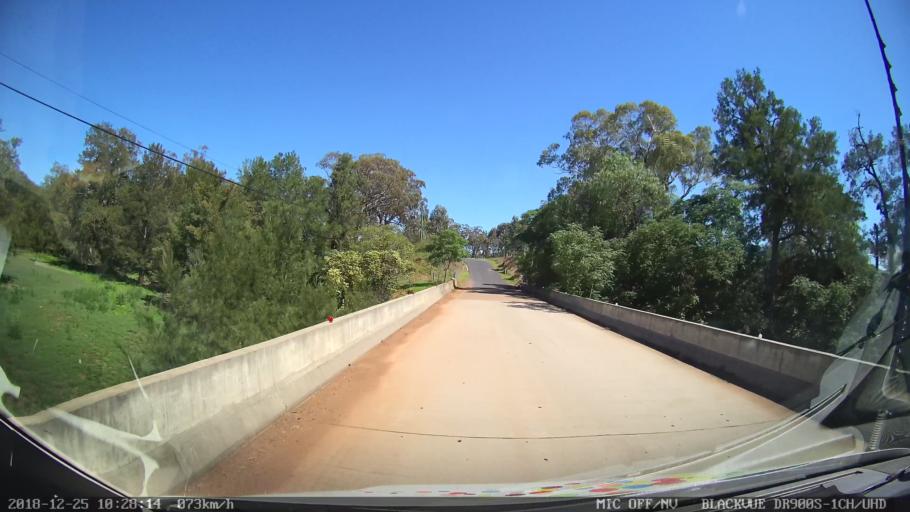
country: AU
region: New South Wales
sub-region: Muswellbrook
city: Denman
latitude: -32.3836
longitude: 150.4654
